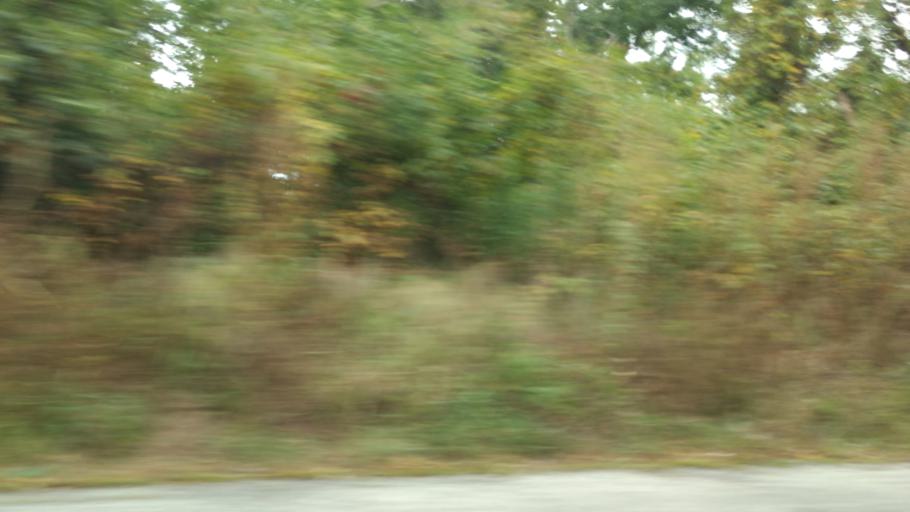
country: US
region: Pennsylvania
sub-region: Westmoreland County
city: Fellsburg
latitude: 40.1931
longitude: -79.8294
